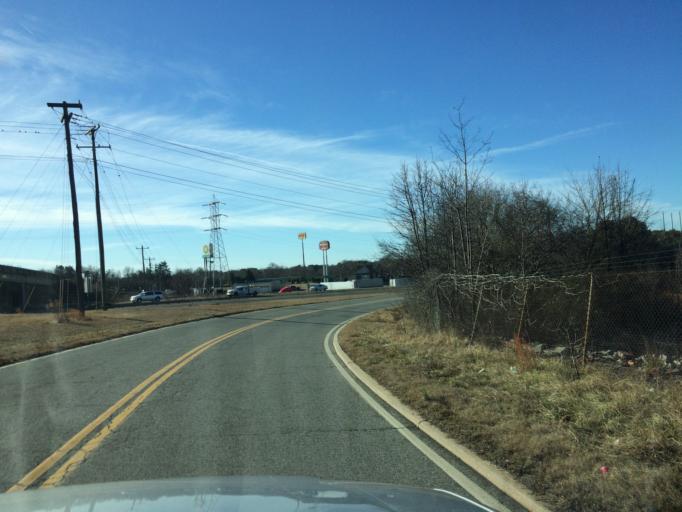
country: US
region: South Carolina
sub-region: Spartanburg County
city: Southern Shops
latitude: 34.9712
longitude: -81.9990
